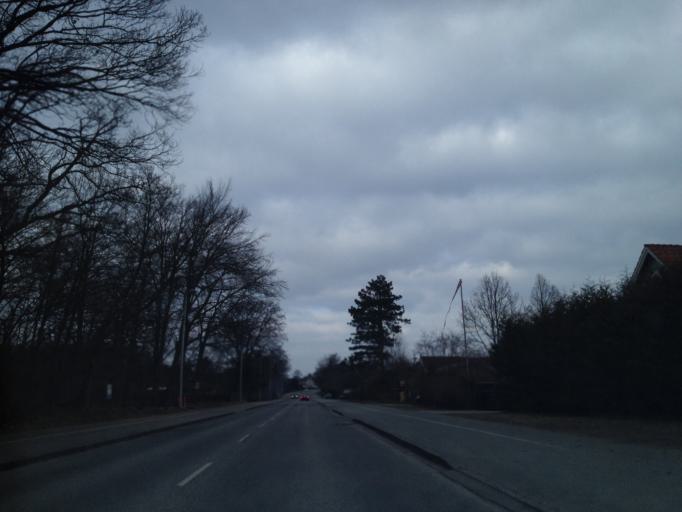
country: DK
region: Capital Region
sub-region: Fredensborg Kommune
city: Humlebaek
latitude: 55.9767
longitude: 12.5441
